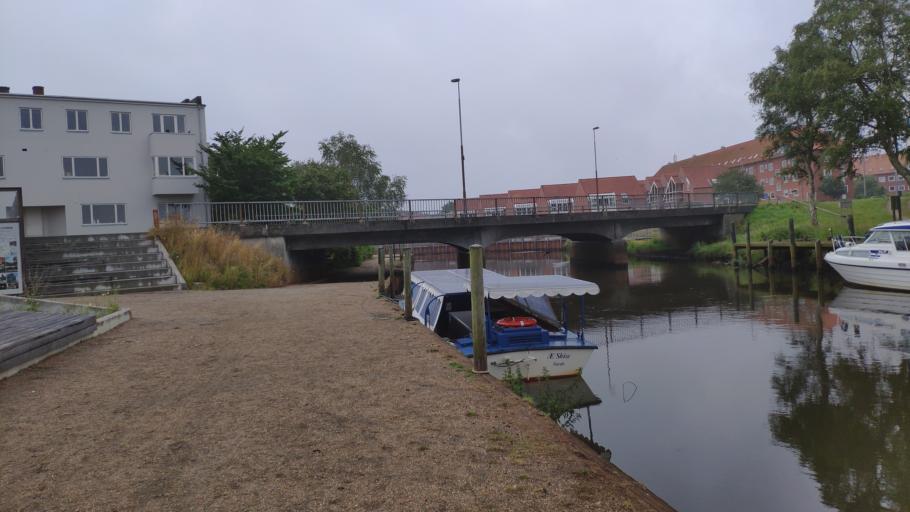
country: DK
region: South Denmark
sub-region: Varde Kommune
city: Varde
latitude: 55.6182
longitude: 8.4814
